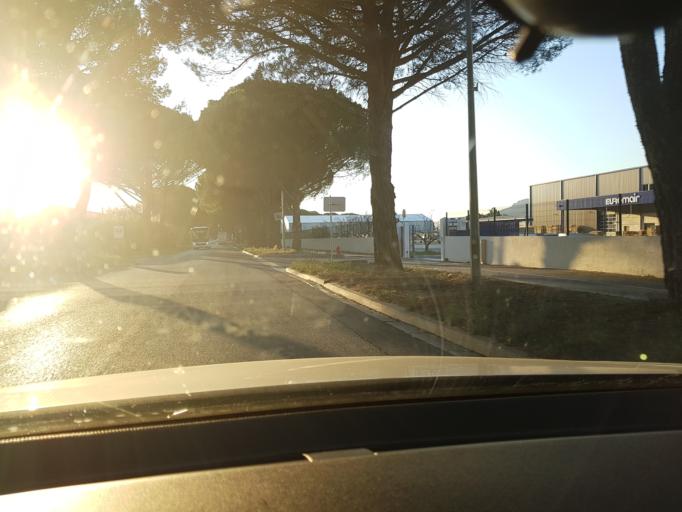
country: FR
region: Provence-Alpes-Cote d'Azur
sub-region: Departement des Bouches-du-Rhone
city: Rousset
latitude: 43.4686
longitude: 5.6108
